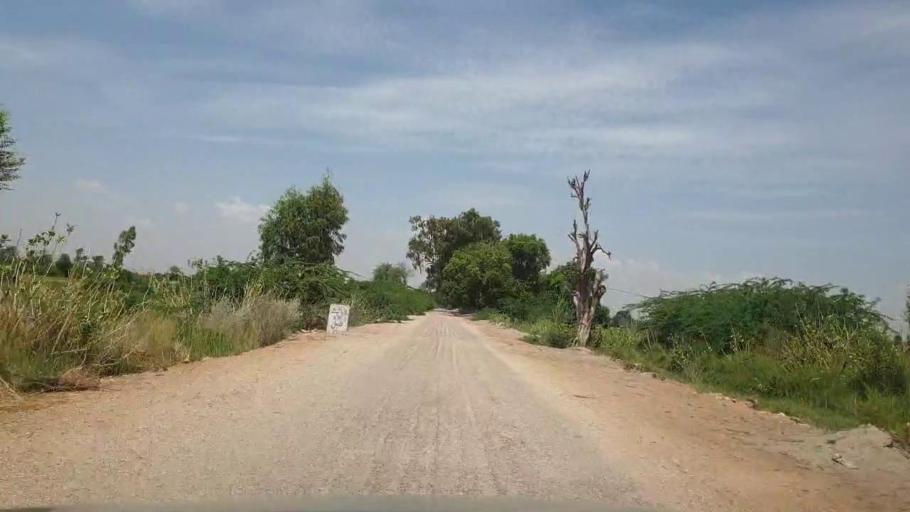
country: PK
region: Sindh
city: Bozdar
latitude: 27.0834
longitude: 68.9767
